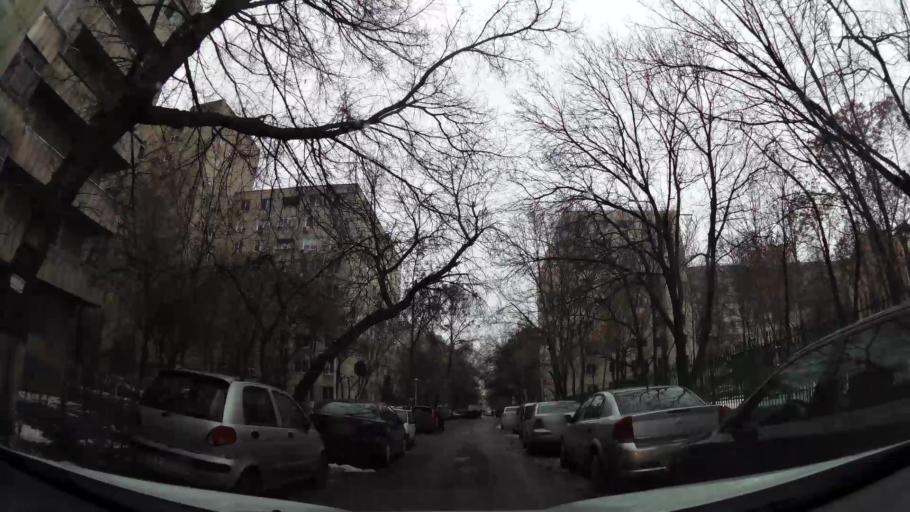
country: RO
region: Ilfov
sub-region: Comuna Chiajna
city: Rosu
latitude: 44.4176
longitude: 26.0451
